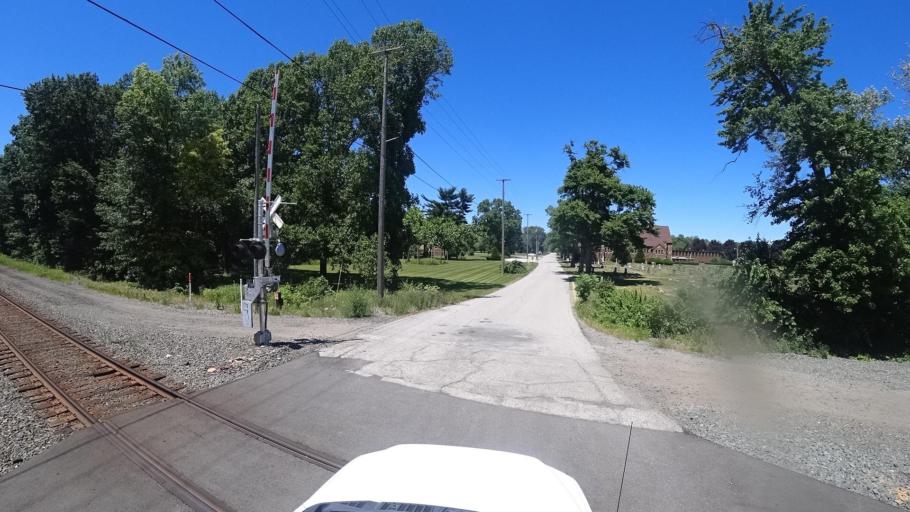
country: US
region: Indiana
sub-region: Porter County
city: Porter
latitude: 41.6146
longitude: -87.0868
